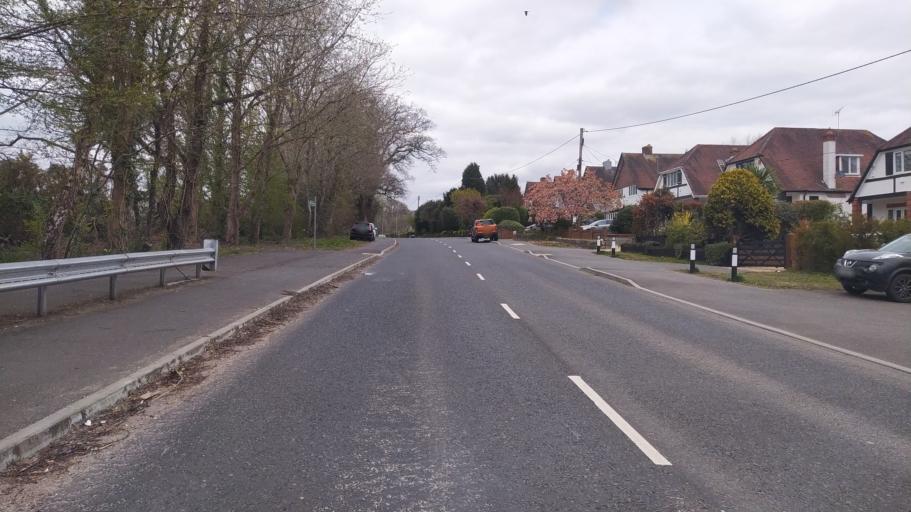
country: GB
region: England
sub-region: Hampshire
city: Totton
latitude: 50.9504
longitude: -1.4669
